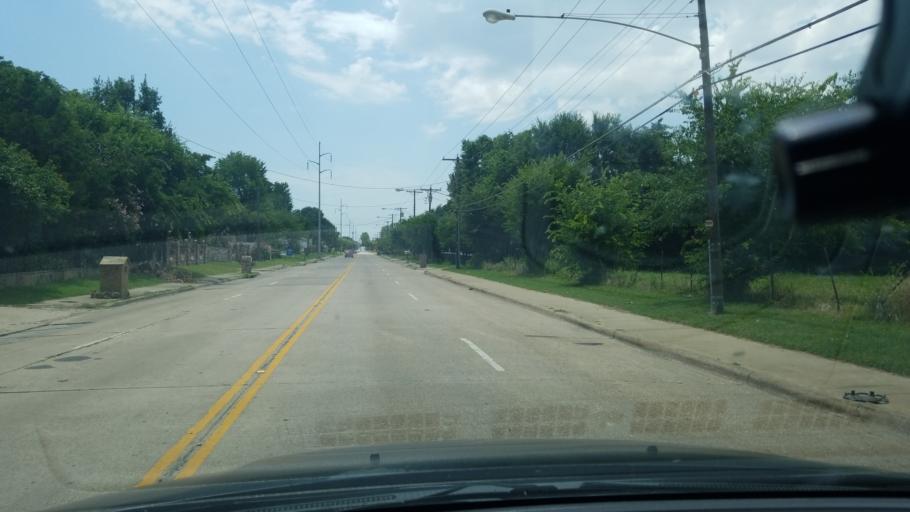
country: US
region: Texas
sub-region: Dallas County
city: Balch Springs
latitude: 32.7464
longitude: -96.6569
